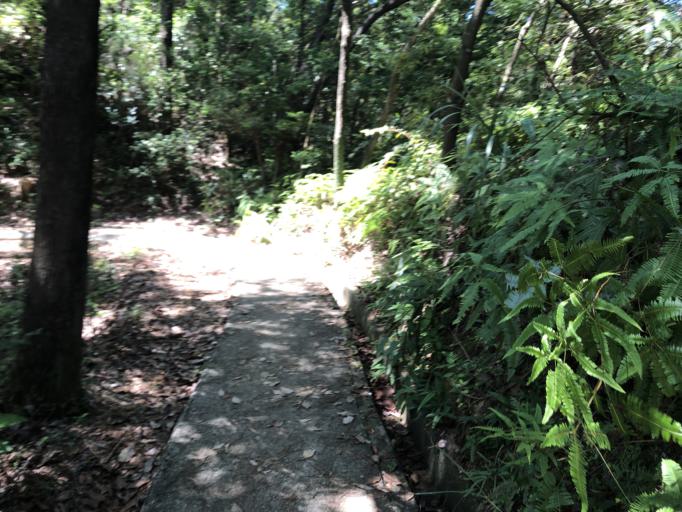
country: HK
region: Tuen Mun
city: Tuen Mun
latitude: 22.2800
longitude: 113.9859
